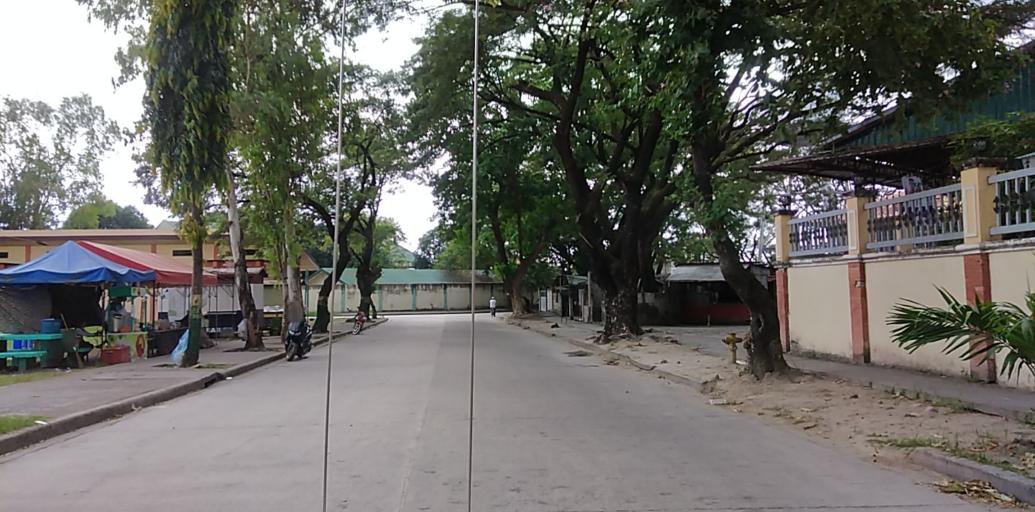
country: PH
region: Central Luzon
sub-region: Province of Pampanga
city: Pio
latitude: 15.0444
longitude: 120.5289
